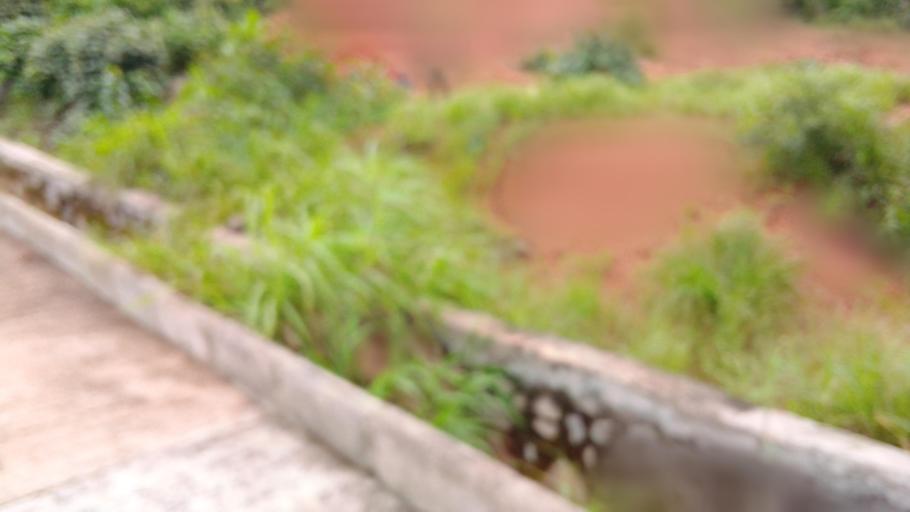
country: SL
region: Eastern Province
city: Kenema
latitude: 7.8509
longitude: -11.1875
